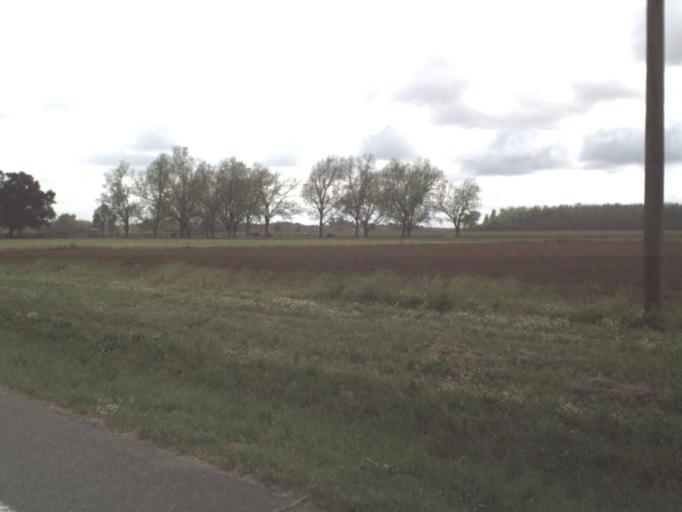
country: US
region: Florida
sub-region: Santa Rosa County
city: Point Baker
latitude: 30.7911
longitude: -87.0924
